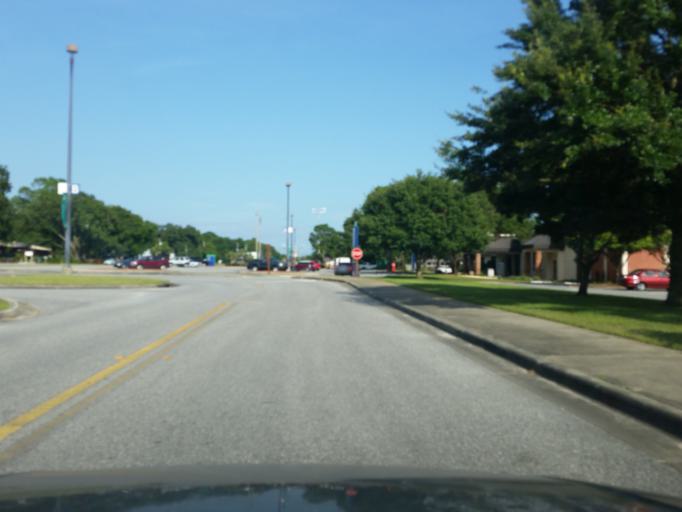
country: US
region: Florida
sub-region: Escambia County
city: Ferry Pass
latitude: 30.4831
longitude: -87.2012
